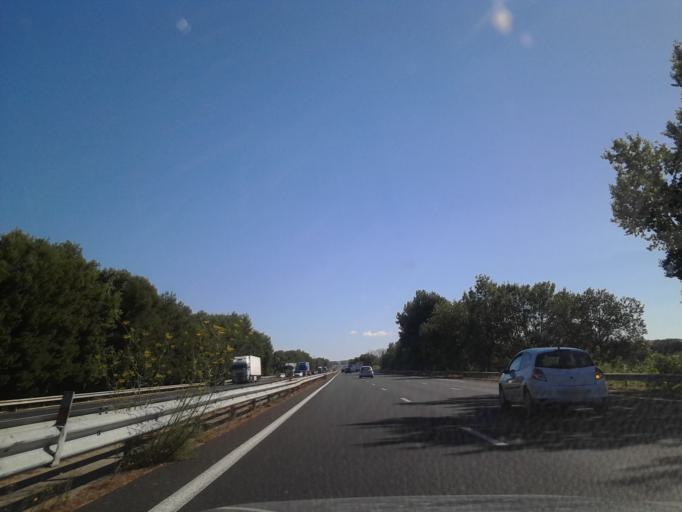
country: FR
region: Languedoc-Roussillon
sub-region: Departement de l'Herault
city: Villeneuve-les-Beziers
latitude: 43.3162
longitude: 3.2598
